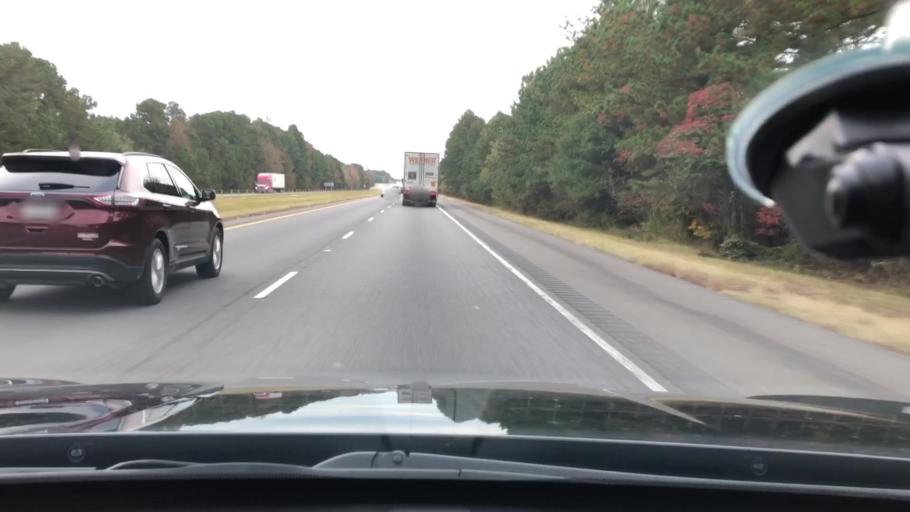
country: US
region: Arkansas
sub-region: Clark County
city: Arkadelphia
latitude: 34.0605
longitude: -93.1280
